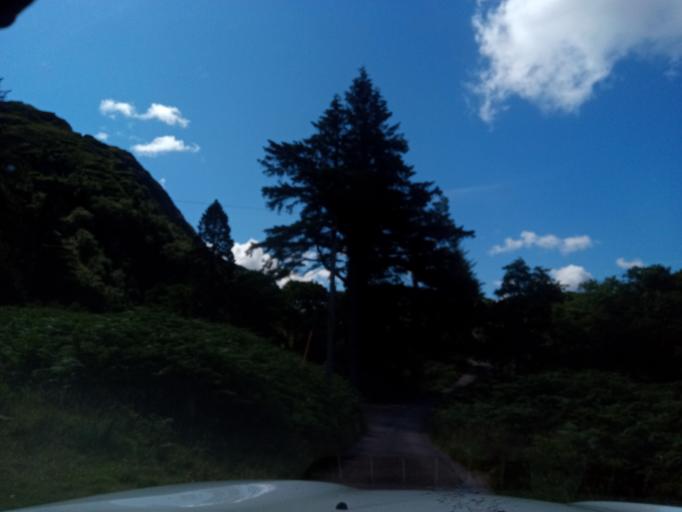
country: GB
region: Scotland
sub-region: Argyll and Bute
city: Isle Of Mull
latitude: 56.7752
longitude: -5.8244
